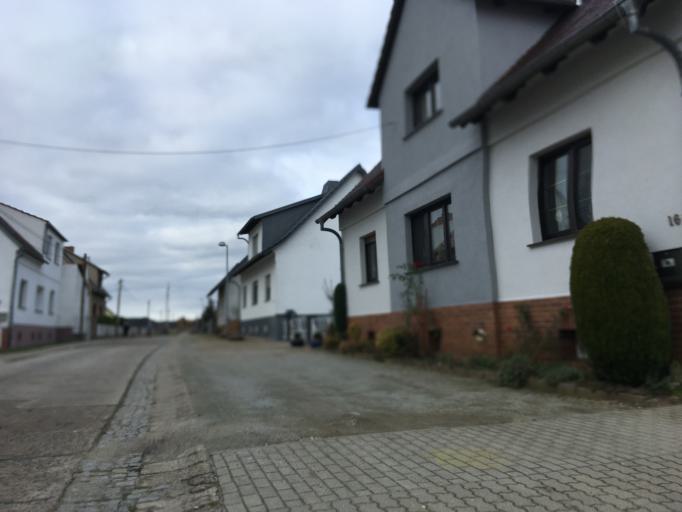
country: DE
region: Brandenburg
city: Schenkendobern
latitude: 51.9819
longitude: 14.5324
